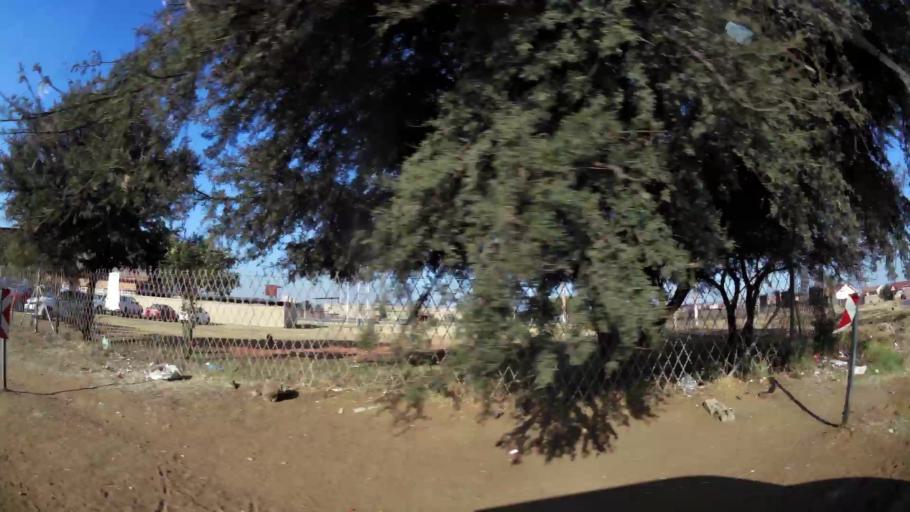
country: ZA
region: Gauteng
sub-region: West Rand District Municipality
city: Randfontein
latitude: -26.1877
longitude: 27.6995
